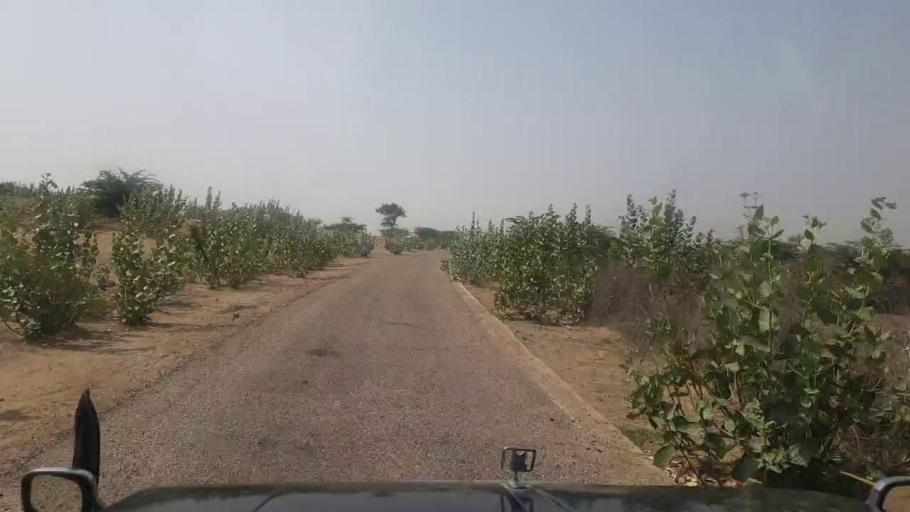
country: PK
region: Sindh
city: Islamkot
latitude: 25.0794
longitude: 70.1541
